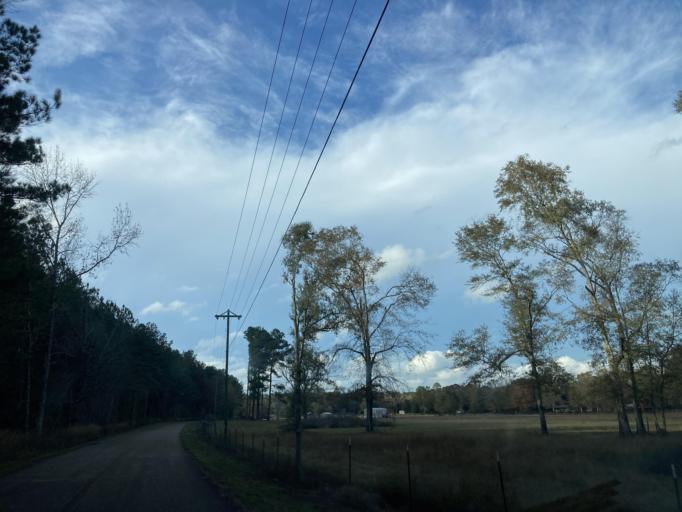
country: US
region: Mississippi
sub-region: Marion County
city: Columbia
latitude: 31.1423
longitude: -89.6413
